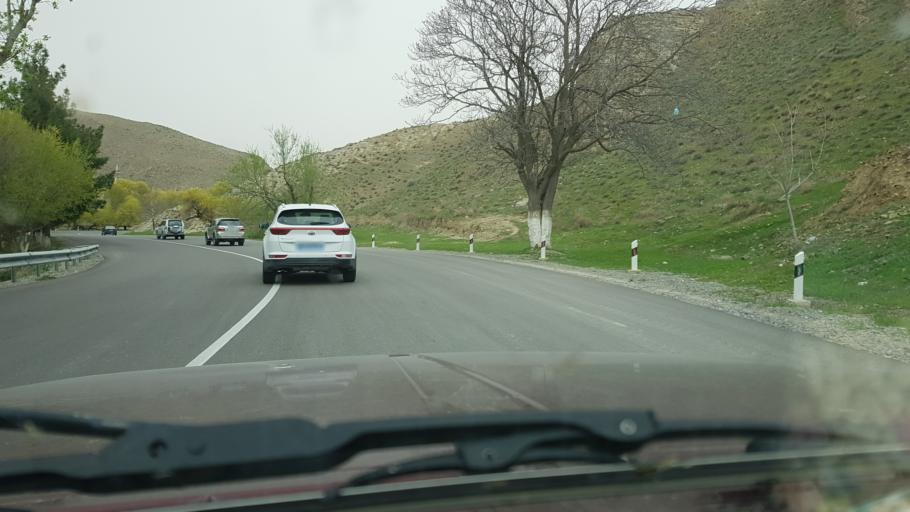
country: TM
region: Ahal
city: Arcabil
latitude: 38.0210
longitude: 58.0055
